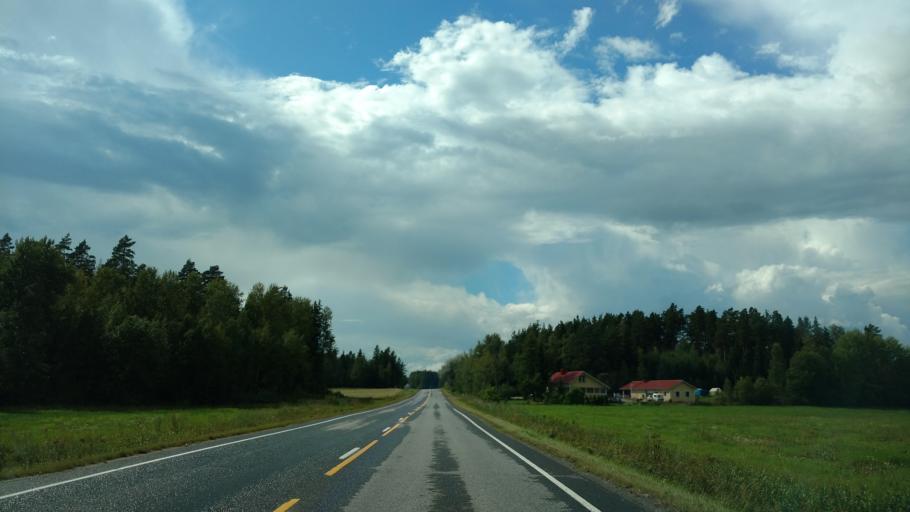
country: FI
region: Varsinais-Suomi
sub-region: Salo
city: Halikko
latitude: 60.3773
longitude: 22.9454
